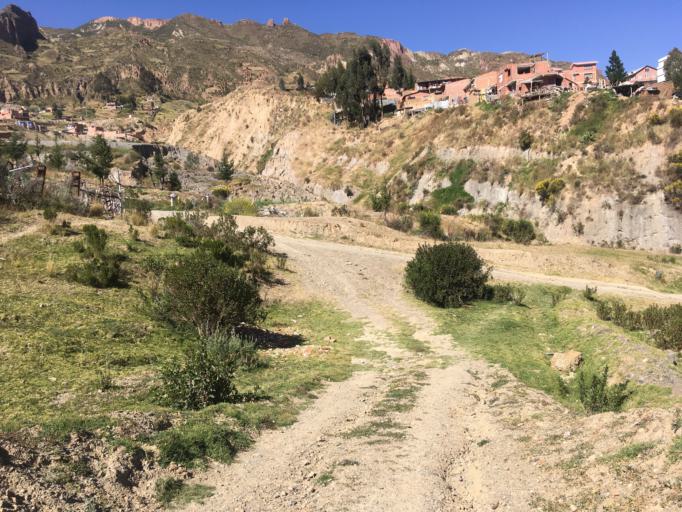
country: BO
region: La Paz
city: La Paz
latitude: -16.5436
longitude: -68.0399
